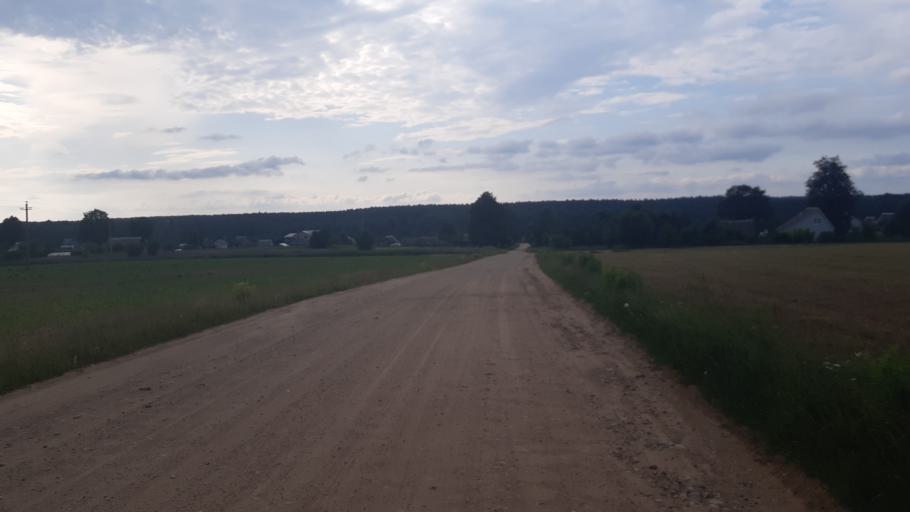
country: BY
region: Minsk
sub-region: Smalyavitski Rayon
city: Oktjabr'skij
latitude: 54.1257
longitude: 28.2044
